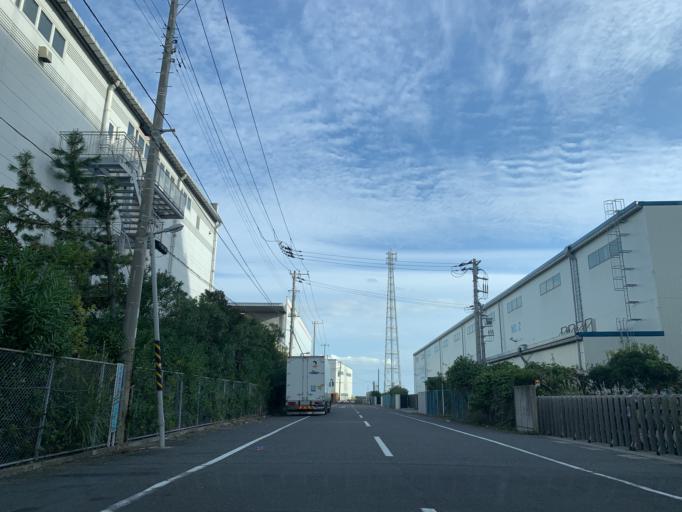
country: JP
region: Tokyo
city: Urayasu
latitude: 35.6265
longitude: 139.9088
